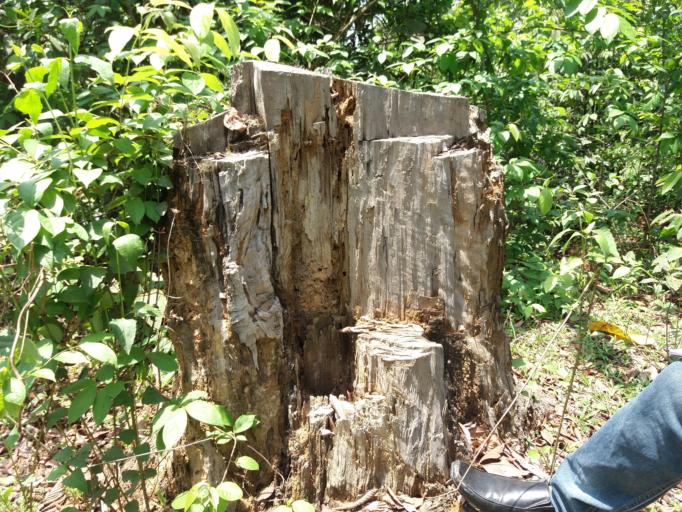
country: BD
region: Chittagong
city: Cox's Bazar
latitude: 21.7062
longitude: 92.0802
